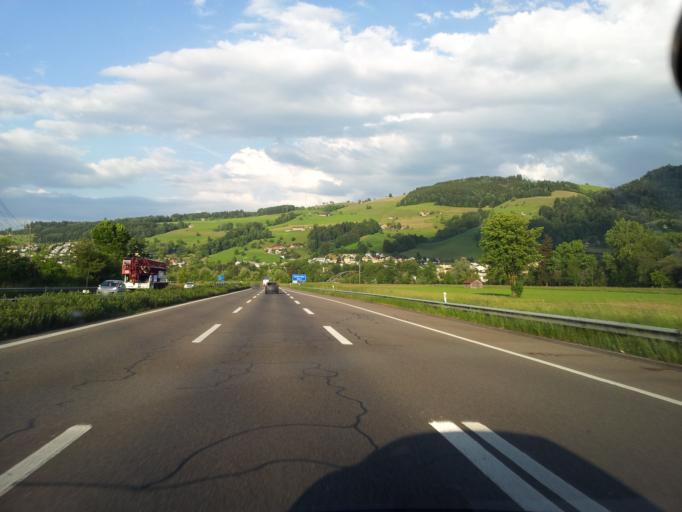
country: CH
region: Lucerne
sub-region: Lucerne-Land District
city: Root
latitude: 47.1190
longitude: 8.3758
